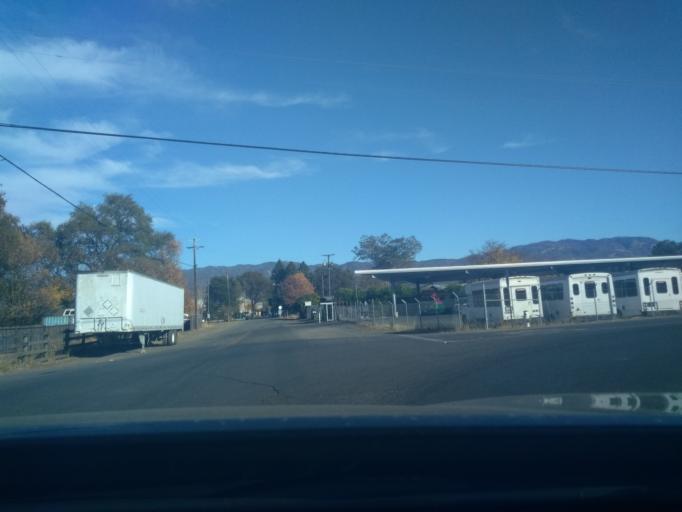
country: US
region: California
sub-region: Mendocino County
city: Talmage
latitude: 39.1122
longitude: -123.1940
